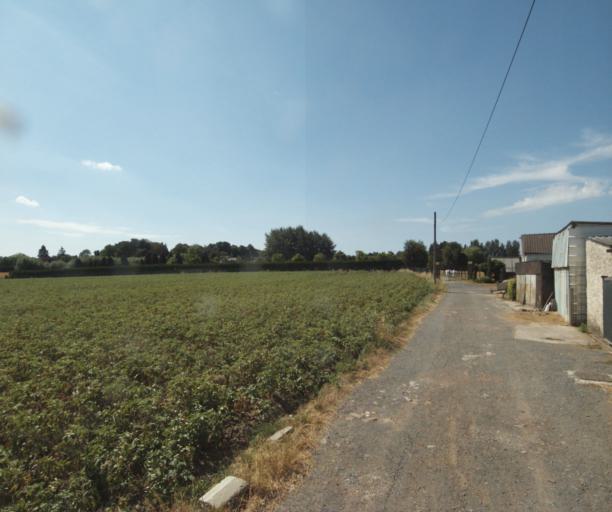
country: FR
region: Nord-Pas-de-Calais
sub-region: Departement du Nord
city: Neuville-en-Ferrain
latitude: 50.7682
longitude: 3.1483
